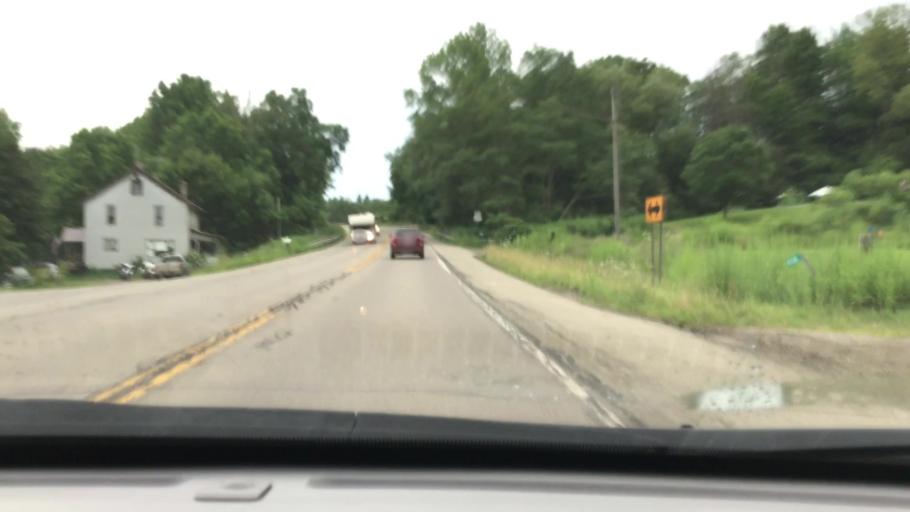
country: US
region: New York
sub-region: Erie County
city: Springville
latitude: 42.4194
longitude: -78.6936
